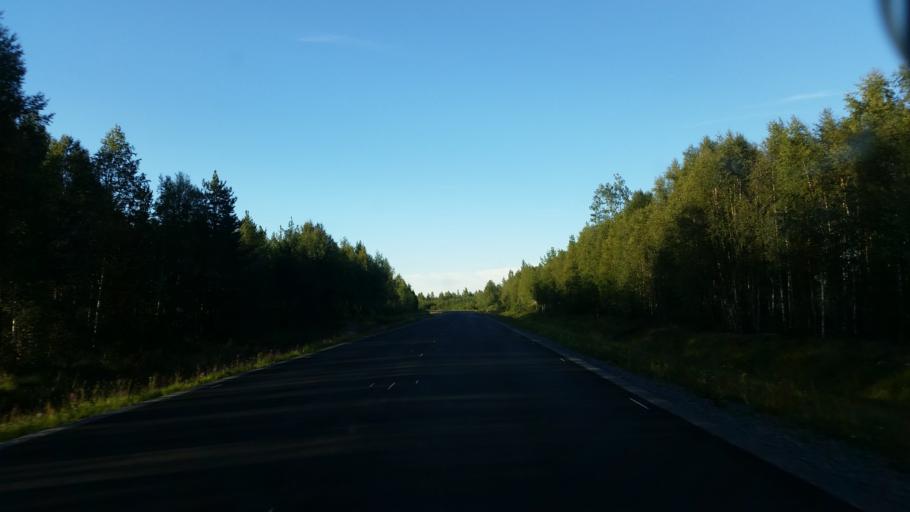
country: SE
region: Vaesterbotten
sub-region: Dorotea Kommun
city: Dorotea
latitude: 64.3325
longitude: 16.6361
